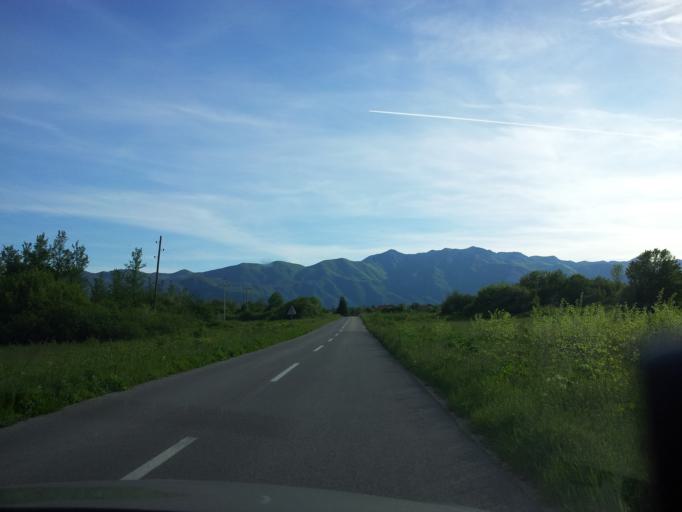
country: HR
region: Zadarska
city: Obrovac
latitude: 44.3762
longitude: 15.6721
